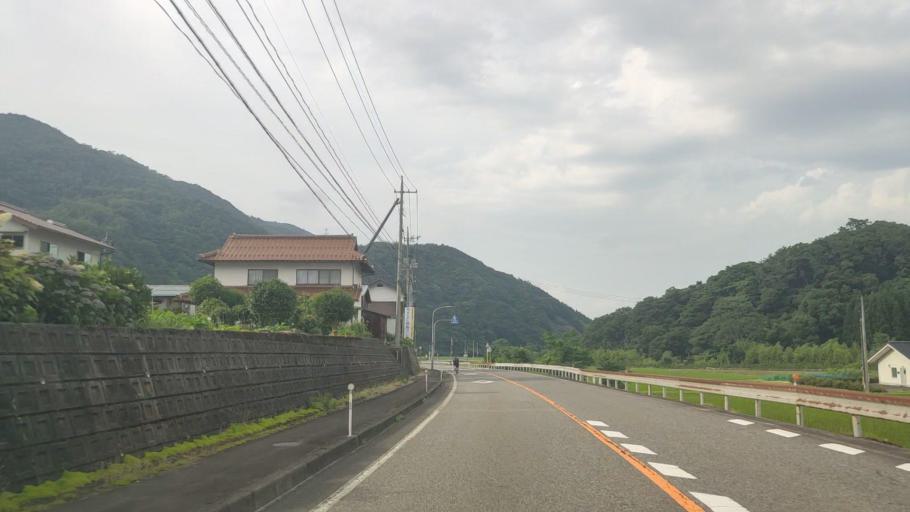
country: JP
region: Tottori
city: Kurayoshi
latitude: 35.3575
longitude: 133.8460
